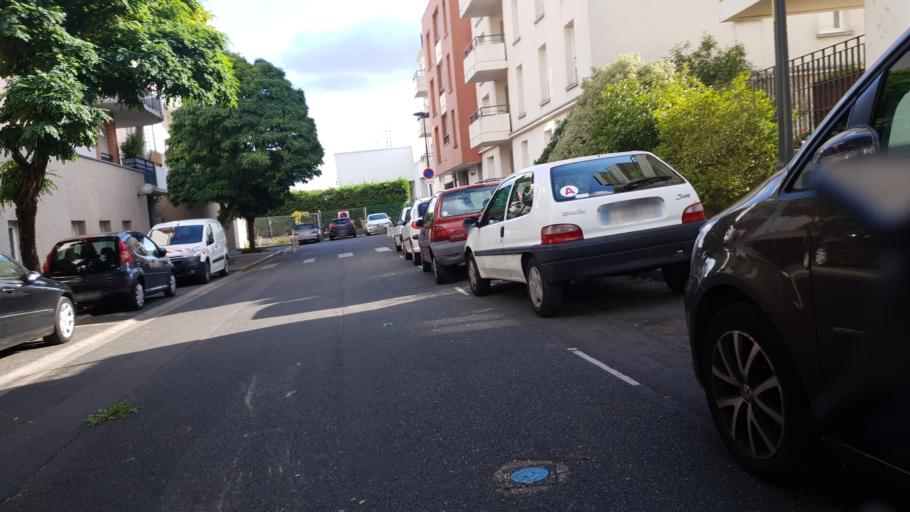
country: FR
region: Centre
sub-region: Departement d'Indre-et-Loire
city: Tours
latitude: 47.3797
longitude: 0.6744
